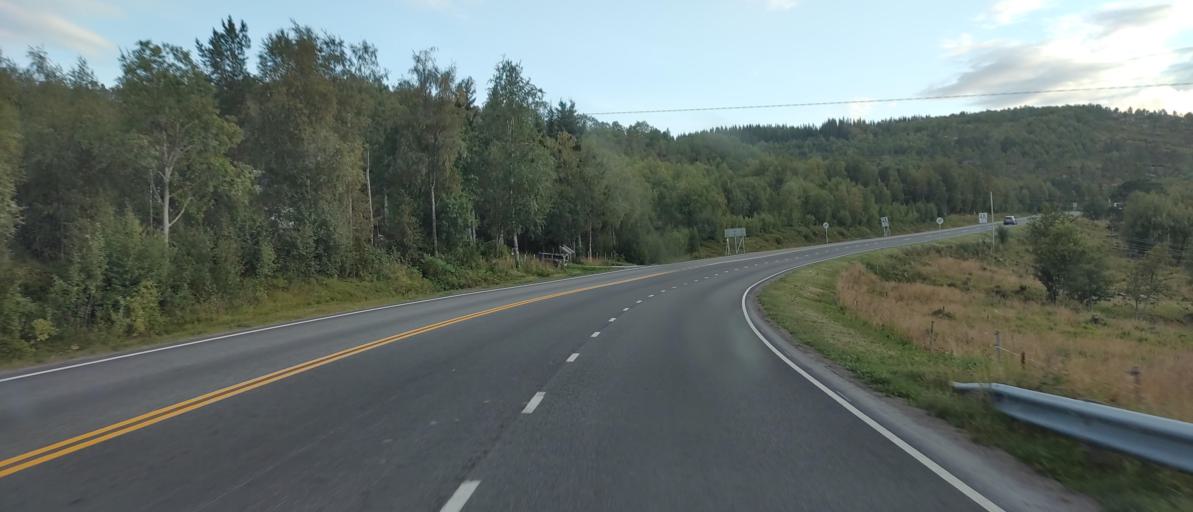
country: NO
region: Nordland
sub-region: Lodingen
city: Lodingen
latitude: 68.2197
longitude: 16.0700
